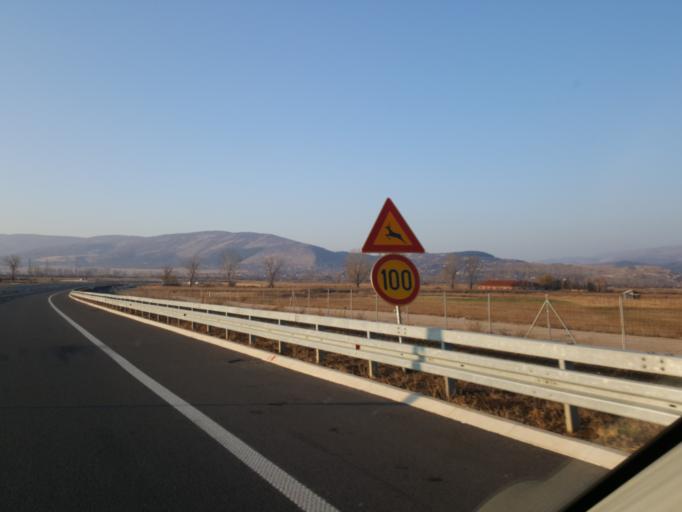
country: RS
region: Central Serbia
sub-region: Pirotski Okrug
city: Pirot
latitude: 43.1312
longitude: 22.5756
